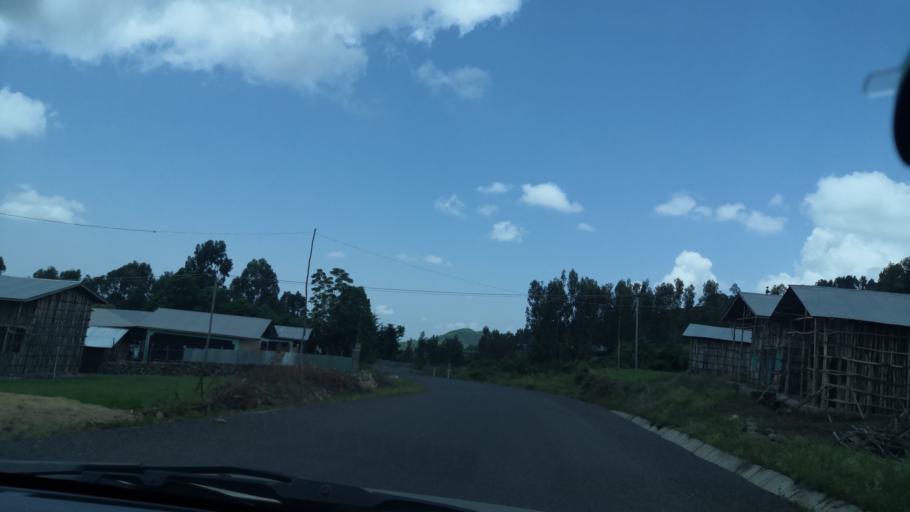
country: ET
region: Amhara
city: Abomsa
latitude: 10.3191
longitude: 39.8738
